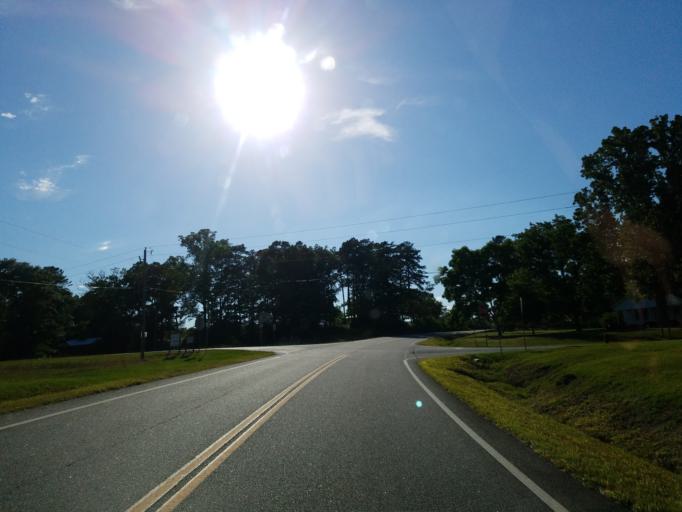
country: US
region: Georgia
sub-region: Gordon County
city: Calhoun
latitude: 34.5882
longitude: -85.0170
